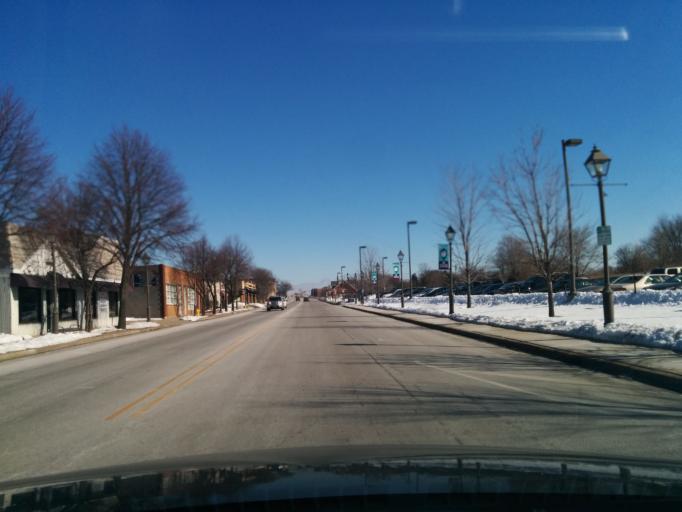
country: US
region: Illinois
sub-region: DuPage County
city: Lombard
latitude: 41.8877
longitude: -88.0163
